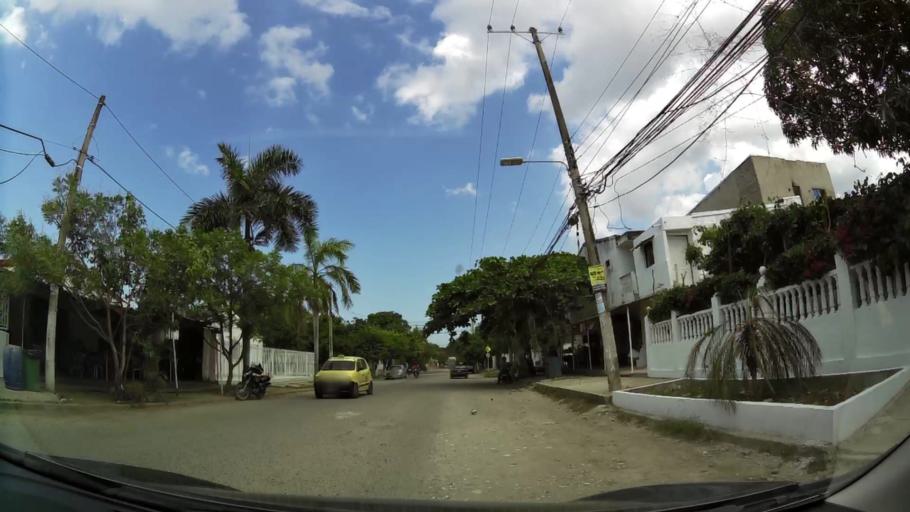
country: CO
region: Bolivar
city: Cartagena
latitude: 10.3722
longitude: -75.4603
